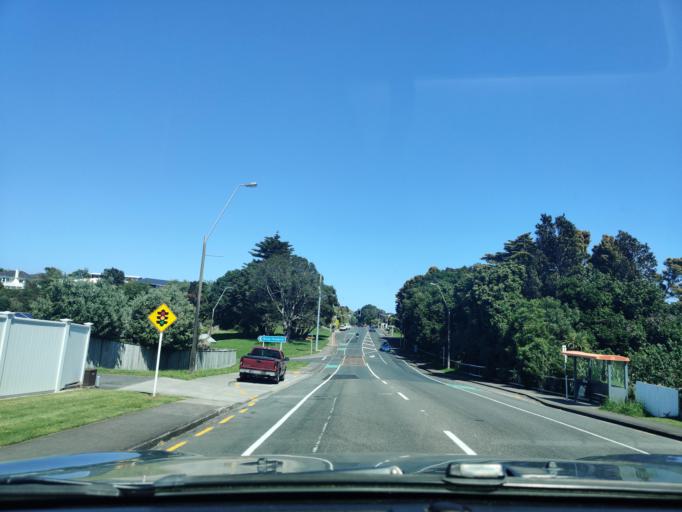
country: NZ
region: Taranaki
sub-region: New Plymouth District
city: New Plymouth
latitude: -39.0636
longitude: 174.0549
